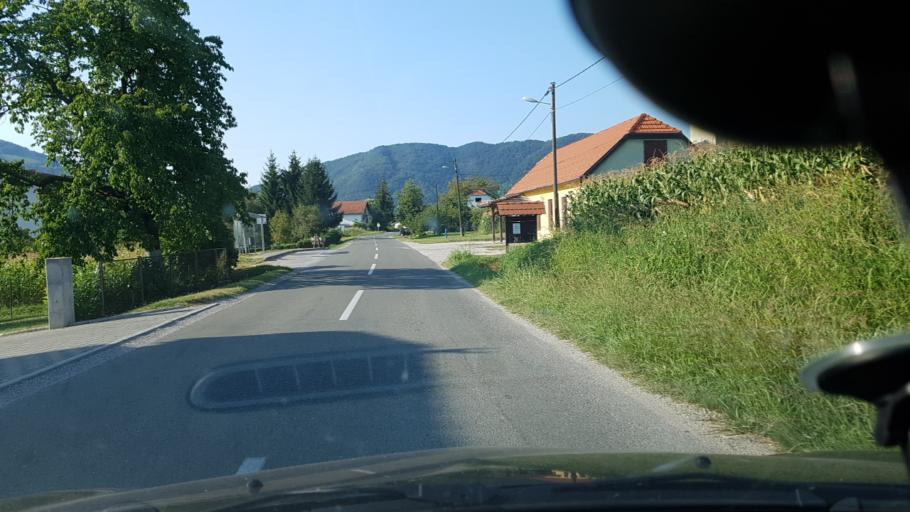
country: SI
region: Bistrica ob Sotli
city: Bistrica ob Sotli
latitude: 46.0320
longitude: 15.7340
